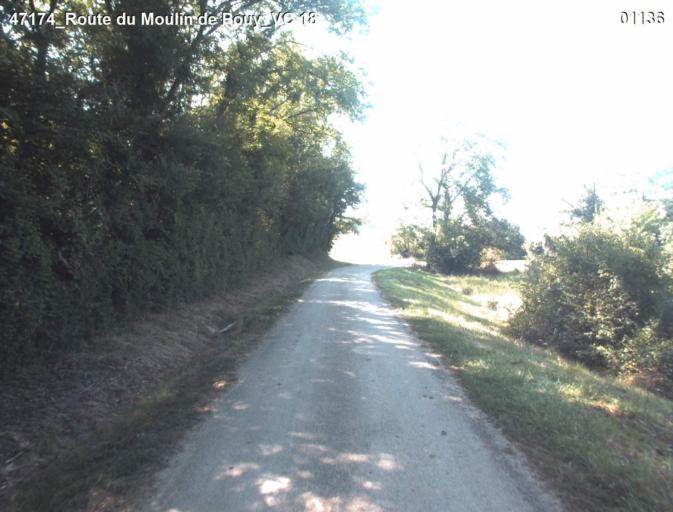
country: FR
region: Aquitaine
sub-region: Departement du Lot-et-Garonne
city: Mezin
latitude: 44.0542
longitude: 0.3188
